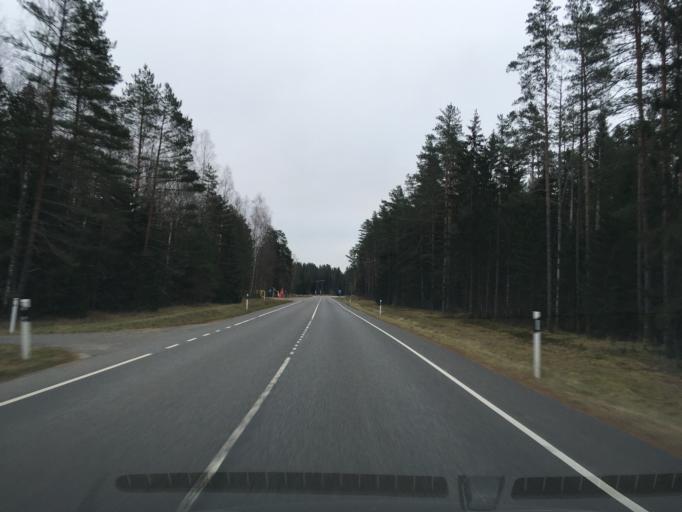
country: EE
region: Laeaene-Virumaa
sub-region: Kadrina vald
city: Kadrina
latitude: 59.4536
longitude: 26.0241
